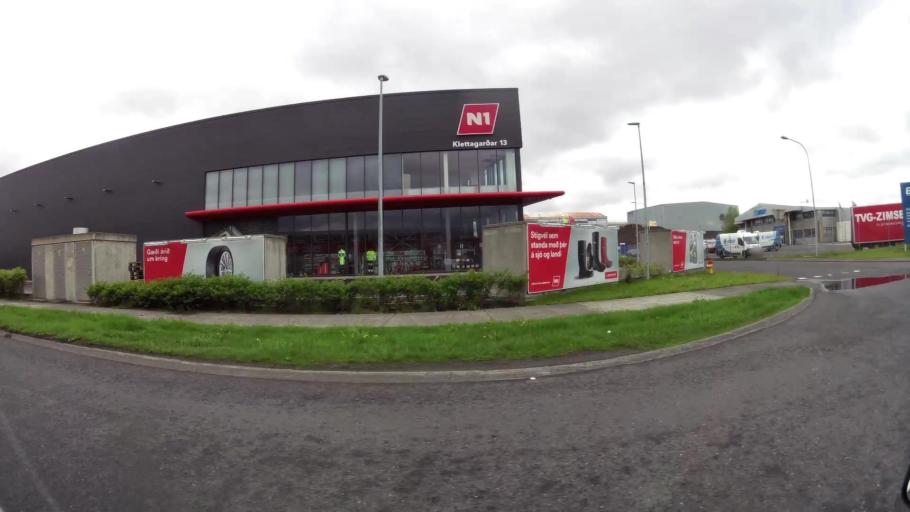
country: IS
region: Capital Region
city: Reykjavik
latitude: 64.1535
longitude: -21.8690
